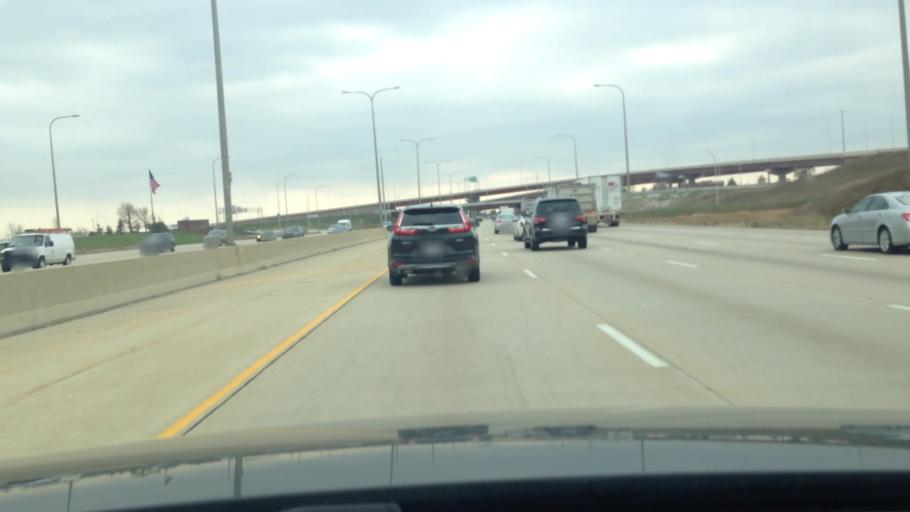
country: US
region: Illinois
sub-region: DuPage County
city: Itasca
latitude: 41.9904
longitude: -88.0235
